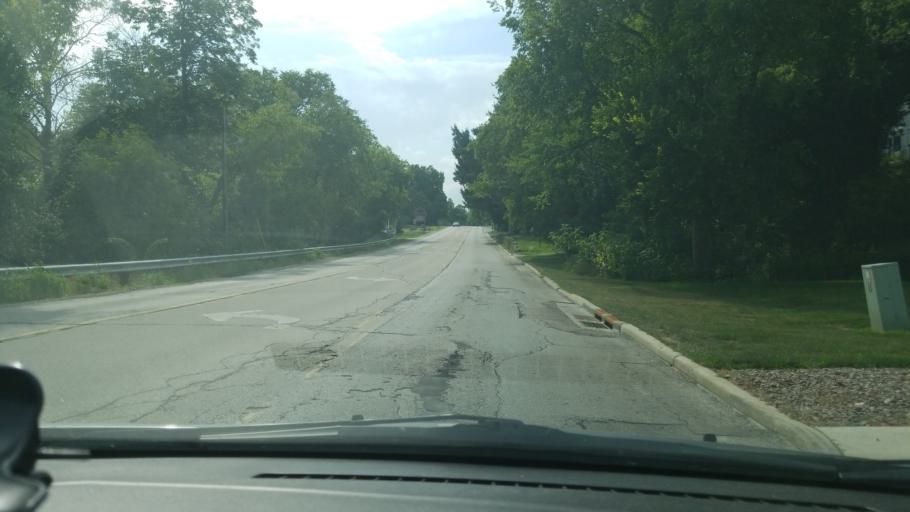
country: US
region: Wisconsin
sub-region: Ozaukee County
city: Cedarburg
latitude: 43.3020
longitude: -87.9673
